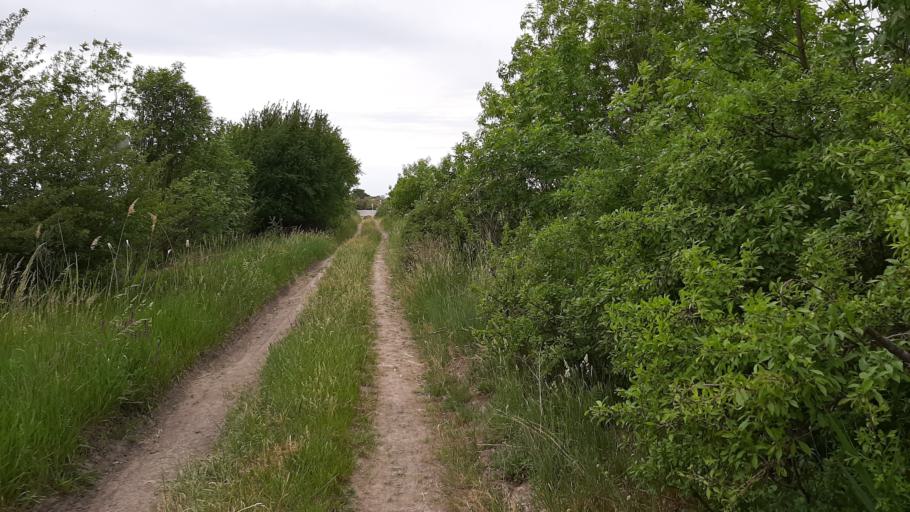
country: RO
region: Timis
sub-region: Comuna Beba Veche
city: Beba Veche
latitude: 46.1423
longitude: 20.2822
